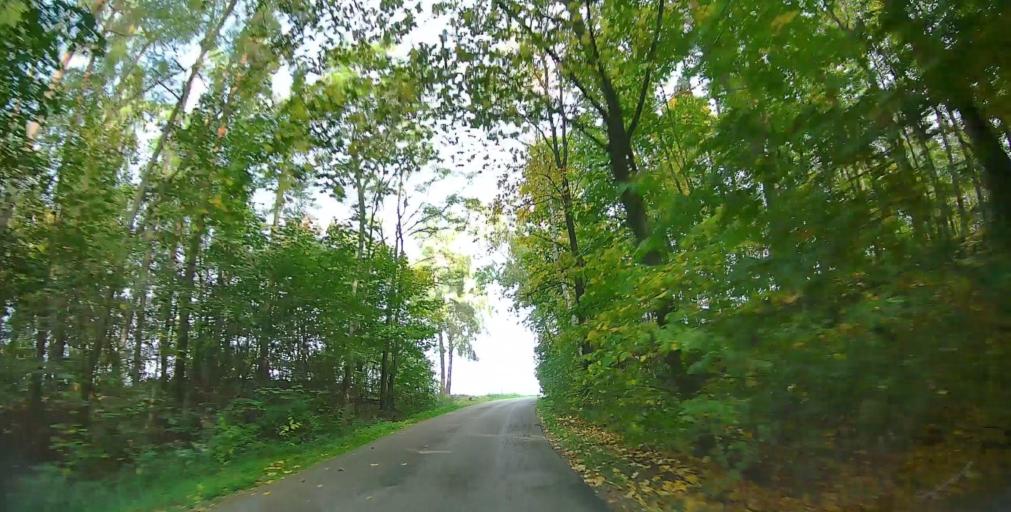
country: PL
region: Masovian Voivodeship
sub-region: Powiat grojecki
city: Mogielnica
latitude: 51.6454
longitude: 20.7556
